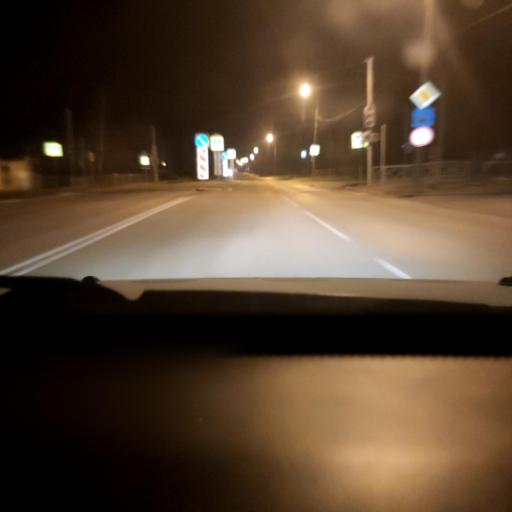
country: RU
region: Perm
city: Polazna
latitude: 58.1167
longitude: 56.4017
